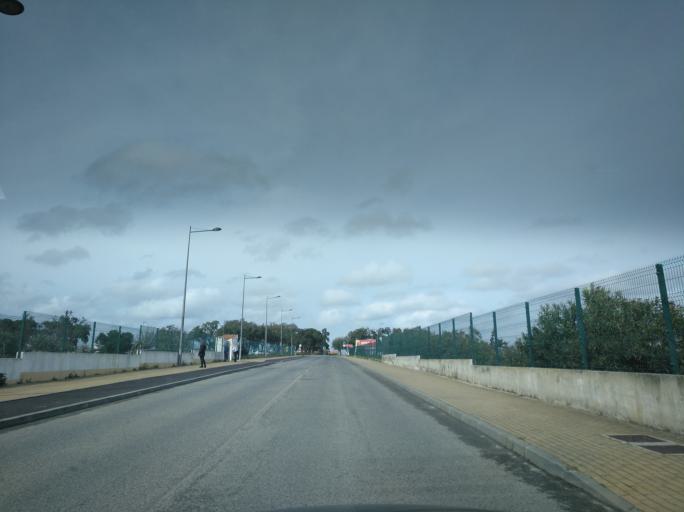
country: PT
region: Setubal
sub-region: Grandola
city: Grandola
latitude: 38.1865
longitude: -8.5634
